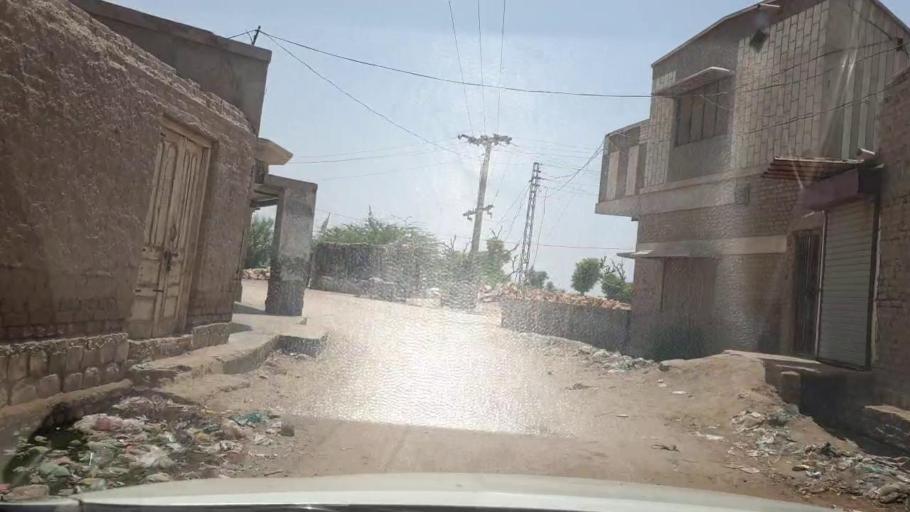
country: PK
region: Sindh
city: Bozdar
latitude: 27.2060
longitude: 68.6663
